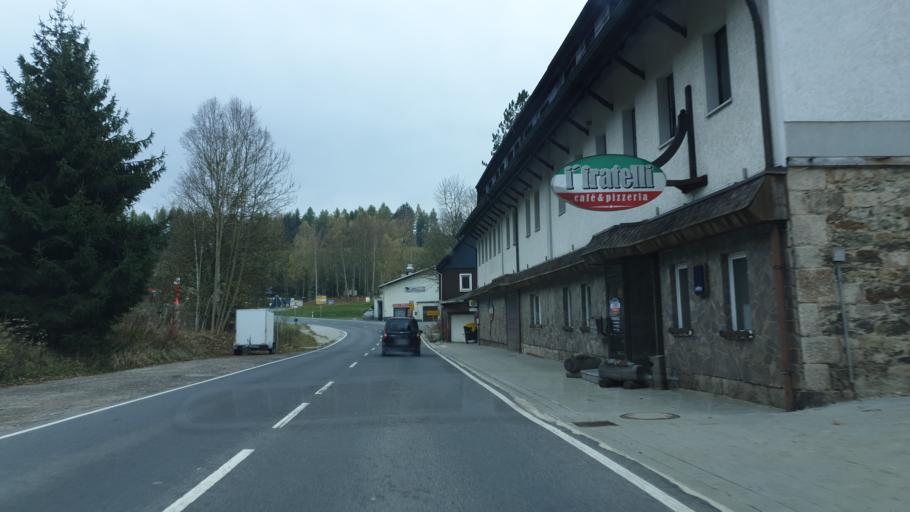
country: DE
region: Saxony
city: Johanngeorgenstadt
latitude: 50.4462
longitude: 12.7279
